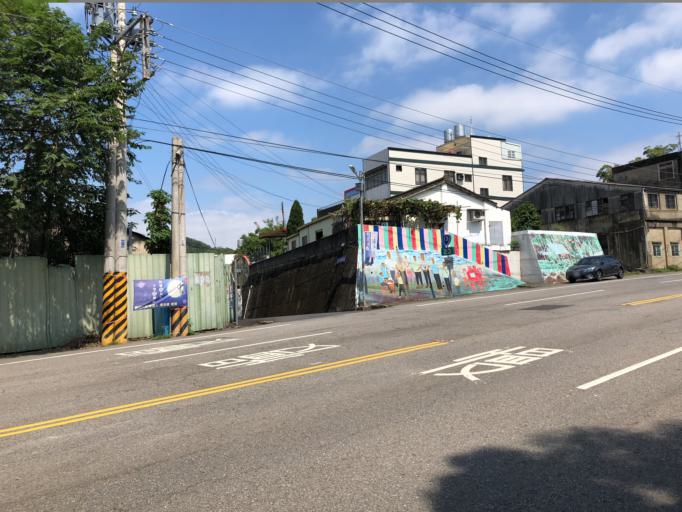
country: TW
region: Taiwan
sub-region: Miaoli
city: Miaoli
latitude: 24.5806
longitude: 120.8653
